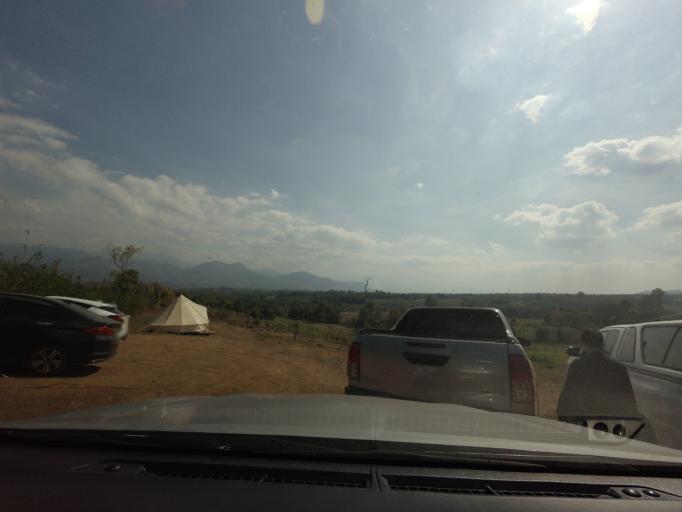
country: TH
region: Mae Hong Son
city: Wiang Nuea
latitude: 19.4005
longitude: 98.4091
